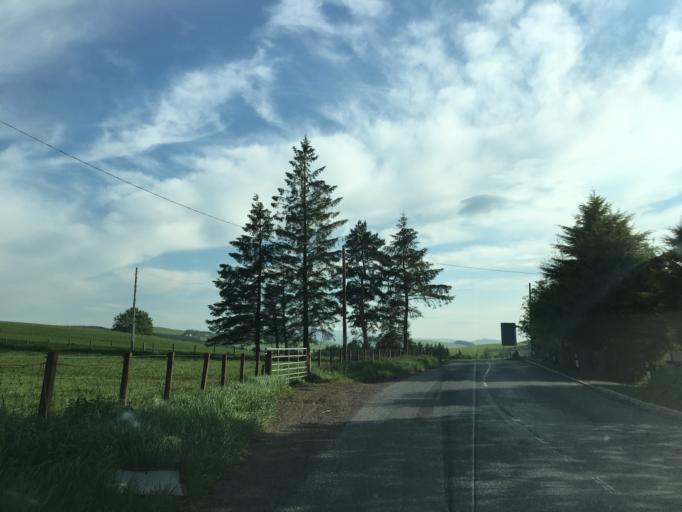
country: GB
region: Scotland
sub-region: South Lanarkshire
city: Biggar
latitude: 55.6538
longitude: -3.4333
